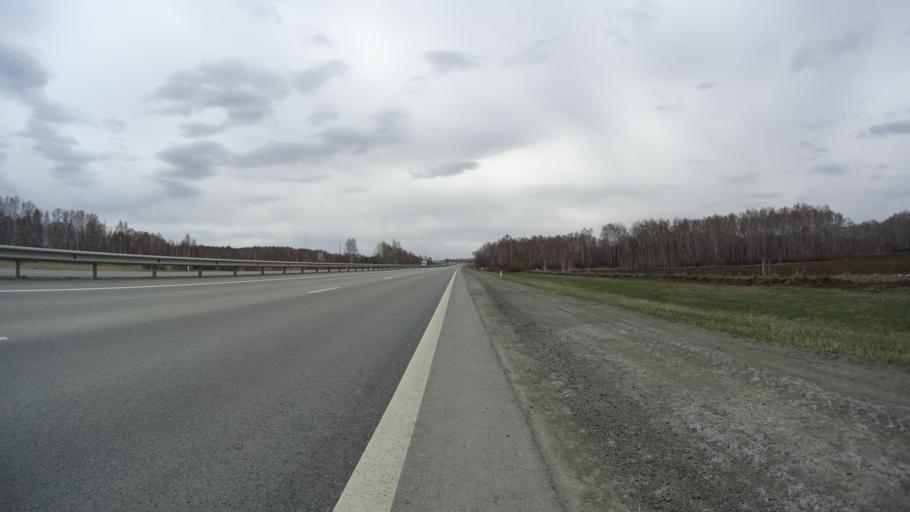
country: RU
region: Chelyabinsk
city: Yemanzhelinka
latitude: 54.8297
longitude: 61.3113
